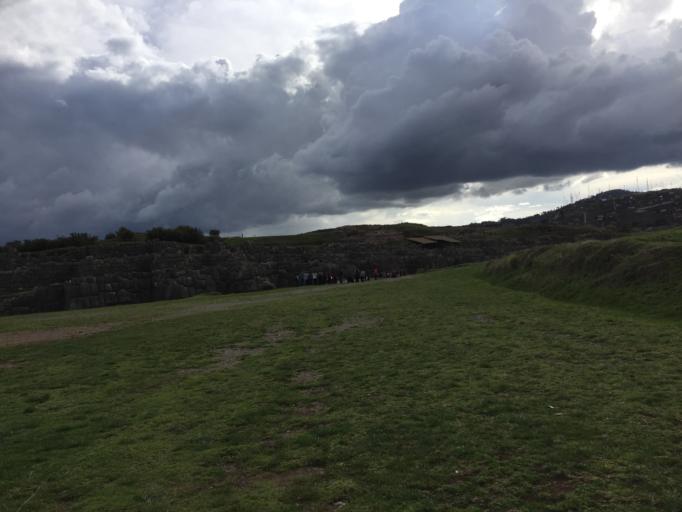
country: PE
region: Cusco
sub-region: Provincia de Cusco
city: Cusco
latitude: -13.5075
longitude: -71.9806
